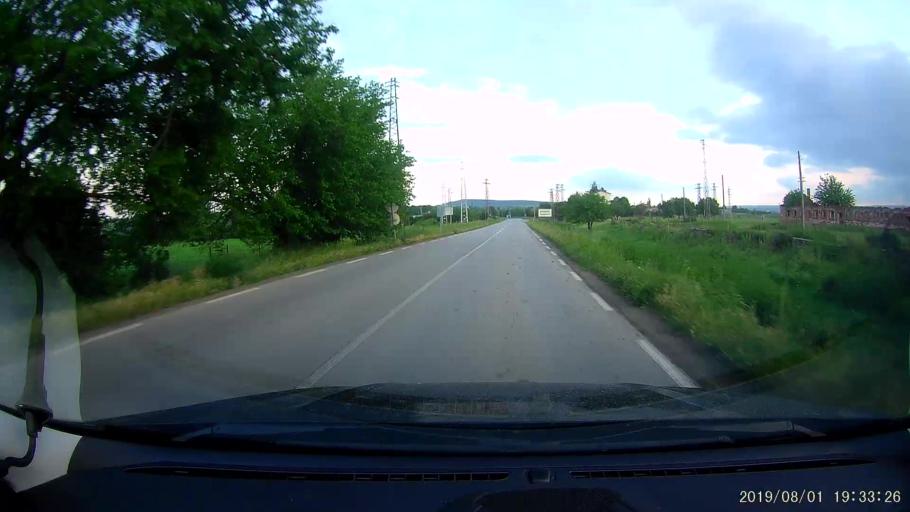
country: BG
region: Burgas
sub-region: Obshtina Sungurlare
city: Sungurlare
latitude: 42.7800
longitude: 26.8766
